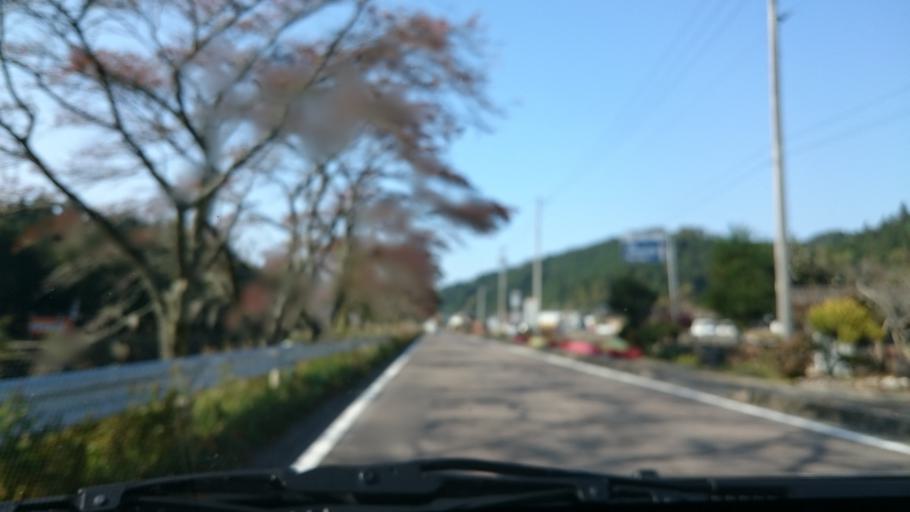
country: JP
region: Gifu
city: Nakatsugawa
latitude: 35.7174
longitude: 137.3641
